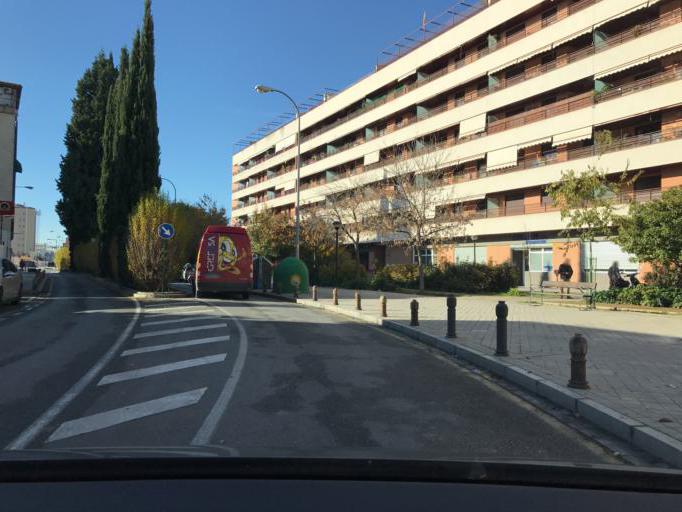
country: ES
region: Andalusia
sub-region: Provincia de Granada
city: Armilla
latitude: 37.1531
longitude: -3.6047
